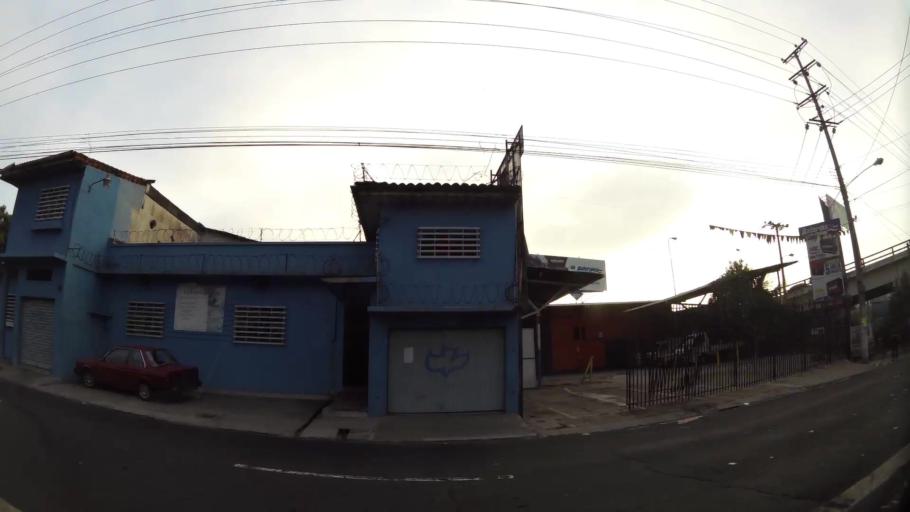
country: SV
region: San Salvador
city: San Salvador
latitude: 13.6927
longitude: -89.2056
